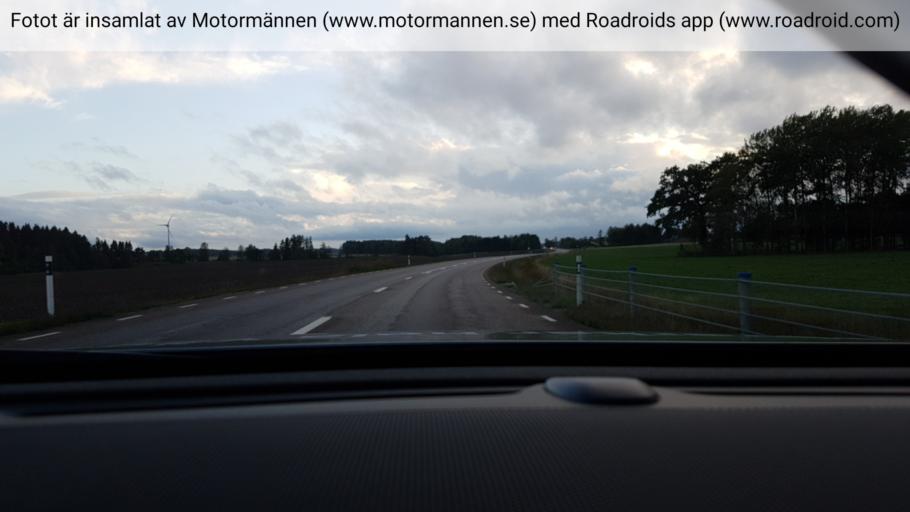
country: SE
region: Vaestra Goetaland
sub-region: Vanersborgs Kommun
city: Bralanda
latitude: 58.5522
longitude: 12.3494
